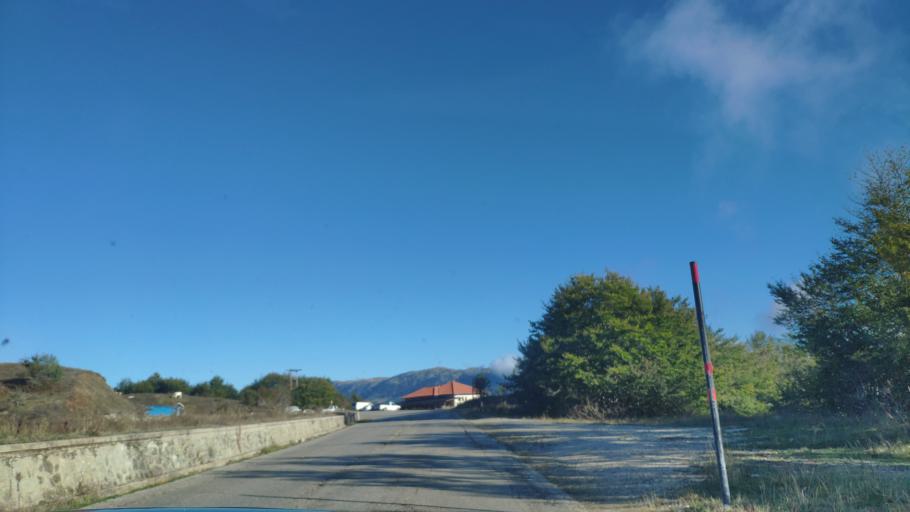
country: GR
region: Epirus
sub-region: Nomos Ioanninon
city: Metsovo
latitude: 39.7797
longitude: 21.1628
